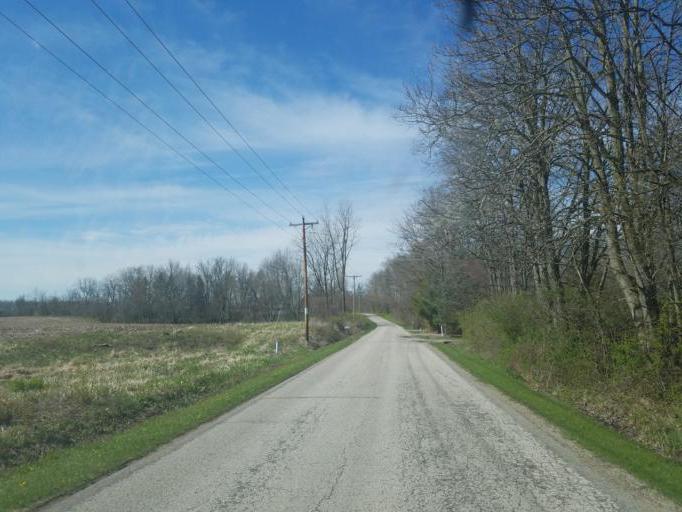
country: US
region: Ohio
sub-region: Delaware County
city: Ashley
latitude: 40.4263
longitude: -82.9901
